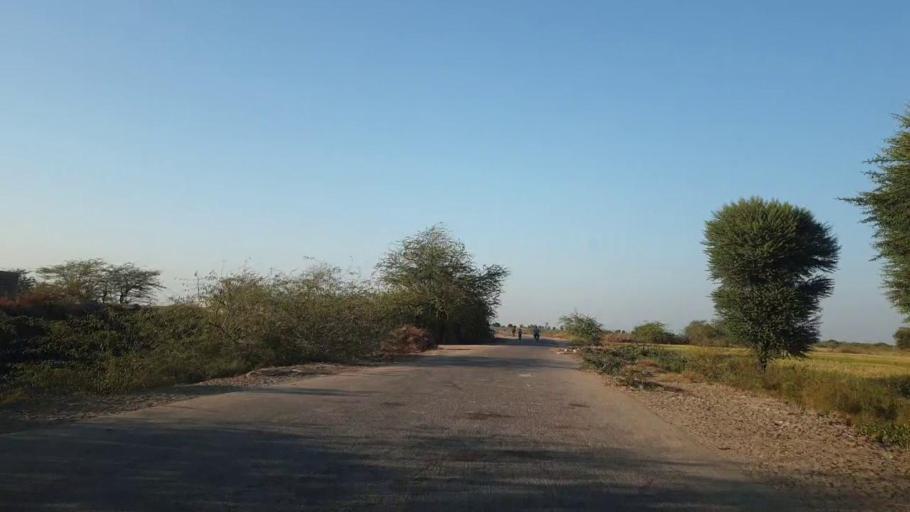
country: PK
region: Sindh
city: Mirpur Khas
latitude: 25.6573
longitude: 69.0937
